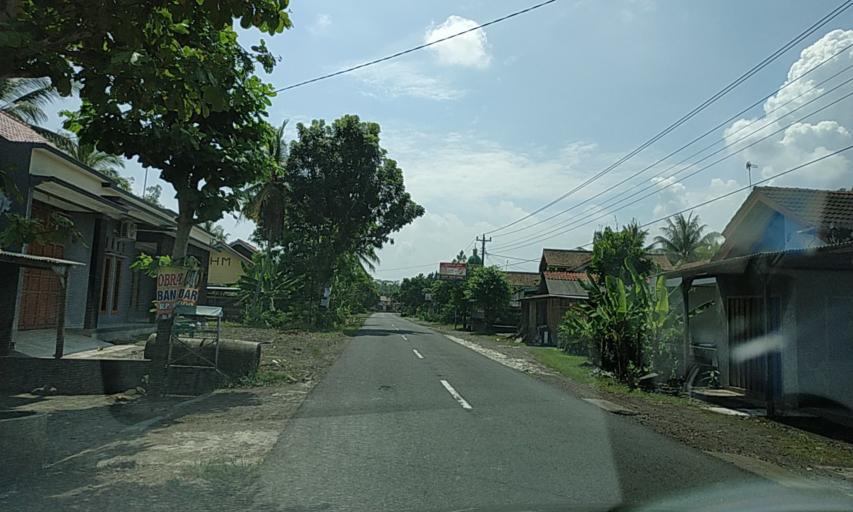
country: ID
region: Central Java
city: Kedungbulu
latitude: -7.5229
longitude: 108.7846
